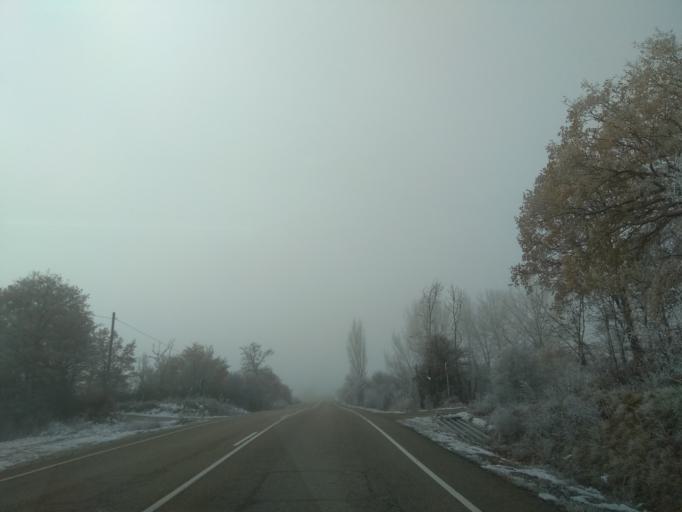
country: ES
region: Castille and Leon
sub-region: Provincia de Burgos
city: Espinosa de los Monteros
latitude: 43.0366
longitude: -3.4962
